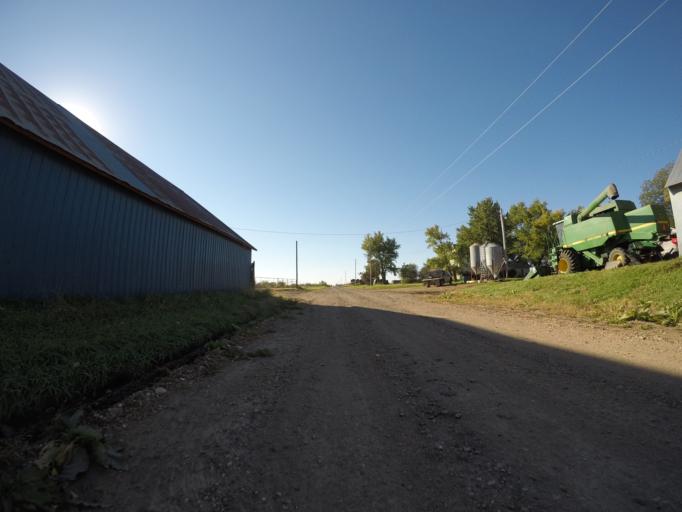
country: US
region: Kansas
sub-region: Morris County
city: Council Grove
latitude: 38.8403
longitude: -96.4829
